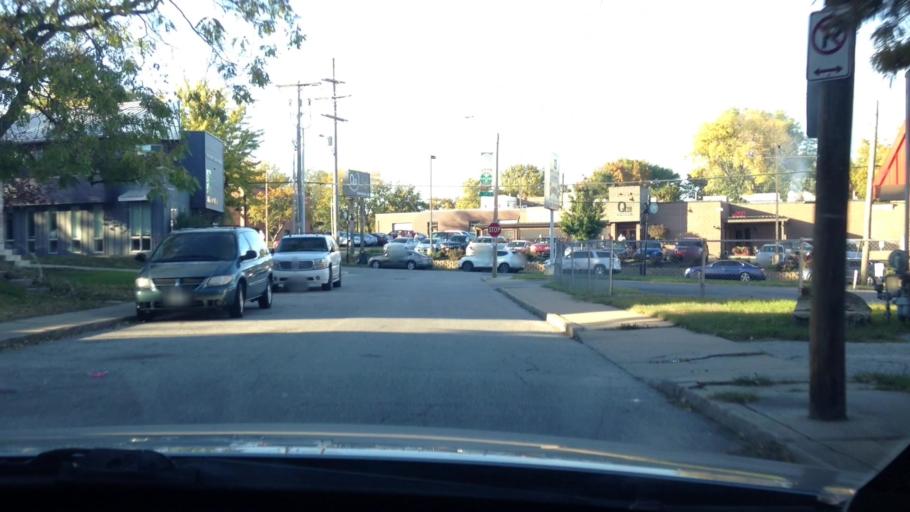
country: US
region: Kansas
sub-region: Johnson County
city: Westwood
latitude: 39.0564
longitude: -94.5981
